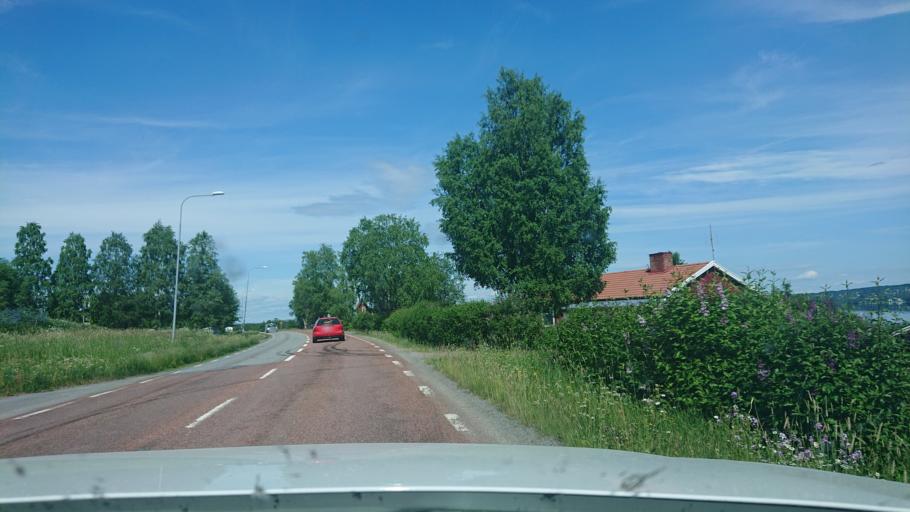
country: SE
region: Jaemtland
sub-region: Stroemsunds Kommun
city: Stroemsund
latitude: 63.8172
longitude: 15.5192
